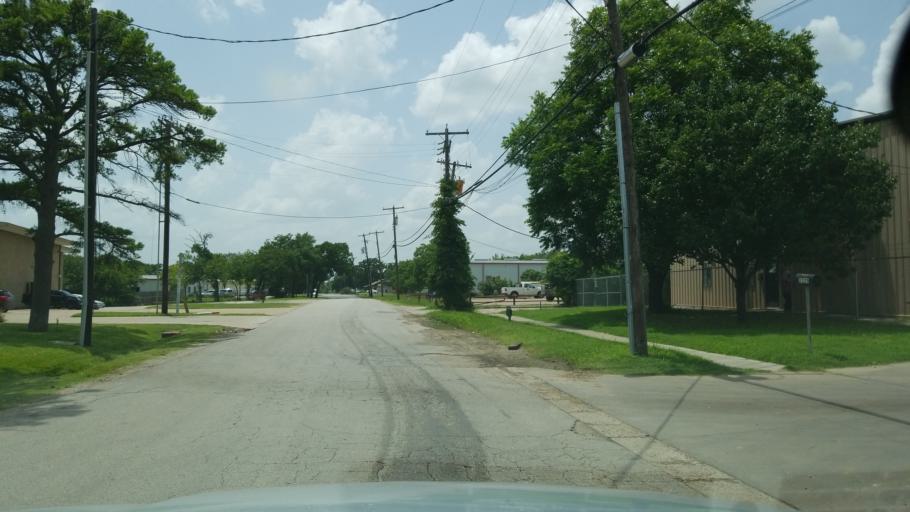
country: US
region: Texas
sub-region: Dallas County
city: Irving
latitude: 32.8259
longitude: -96.9102
